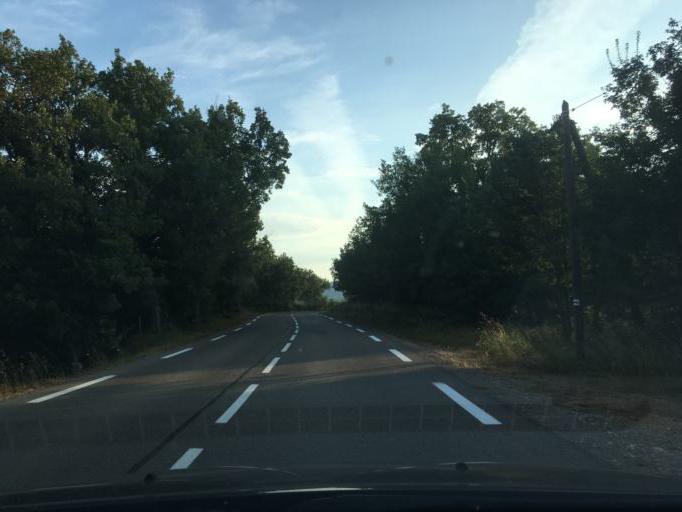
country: FR
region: Provence-Alpes-Cote d'Azur
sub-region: Departement du Var
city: Aups
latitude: 43.7143
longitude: 6.2202
